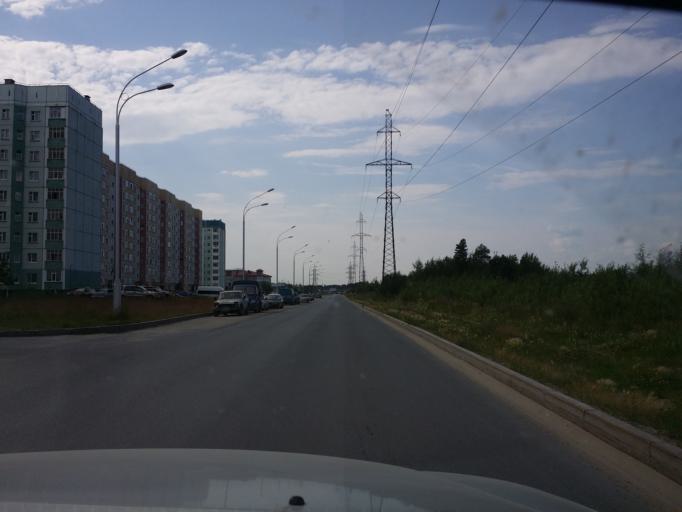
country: RU
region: Khanty-Mansiyskiy Avtonomnyy Okrug
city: Nizhnevartovsk
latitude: 60.9579
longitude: 76.5798
